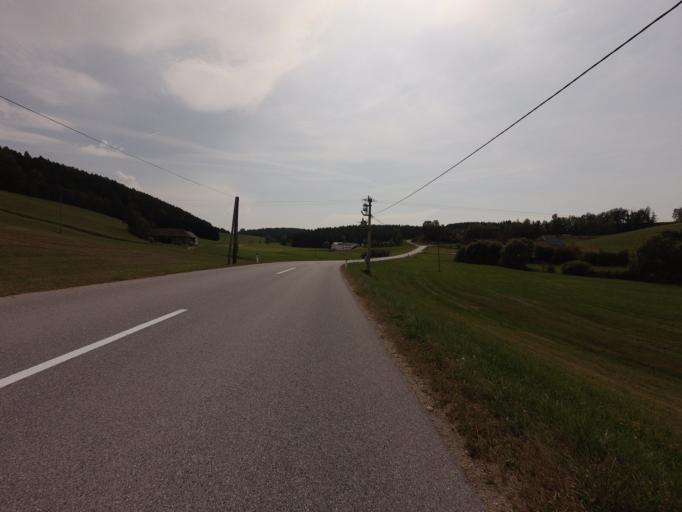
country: AT
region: Upper Austria
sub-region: Politischer Bezirk Urfahr-Umgebung
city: Reichenthal
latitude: 48.5469
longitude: 14.3967
